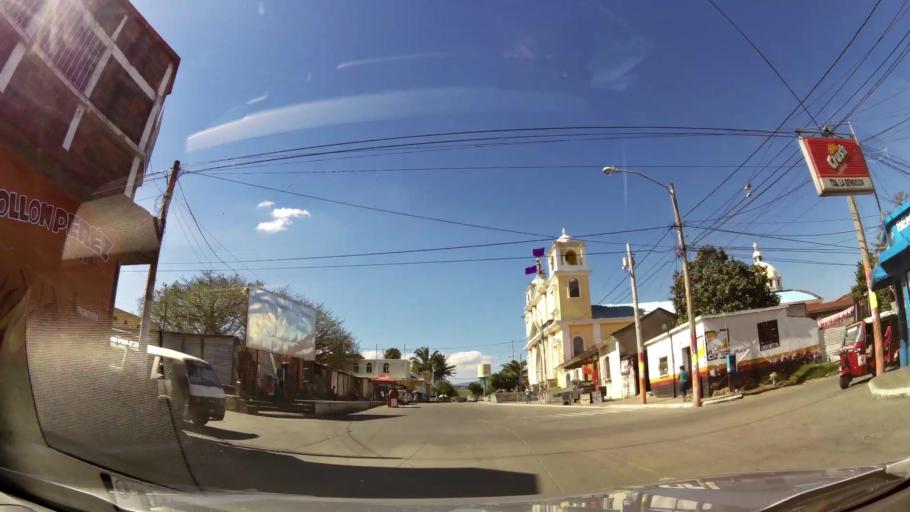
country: GT
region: Guatemala
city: Petapa
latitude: 14.5017
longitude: -90.5602
